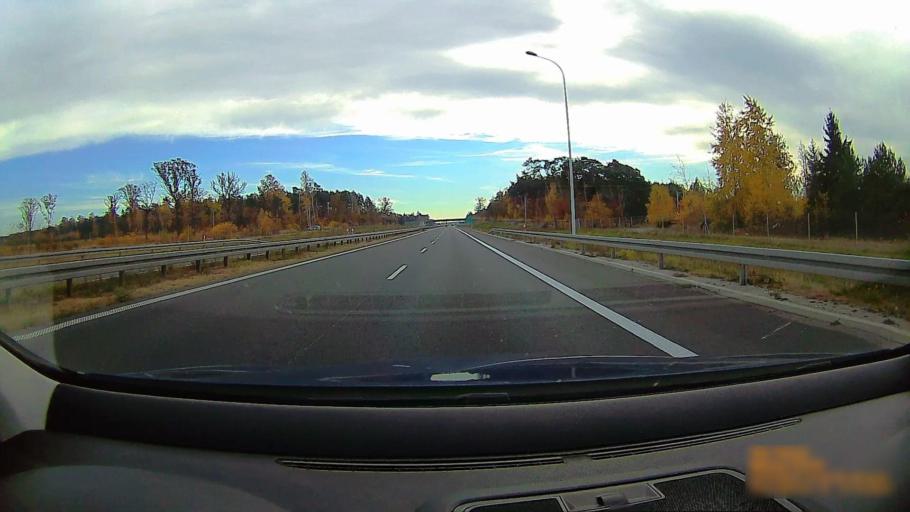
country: PL
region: Greater Poland Voivodeship
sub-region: Powiat ostrowski
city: Ostrow Wielkopolski
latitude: 51.6598
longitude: 17.8612
